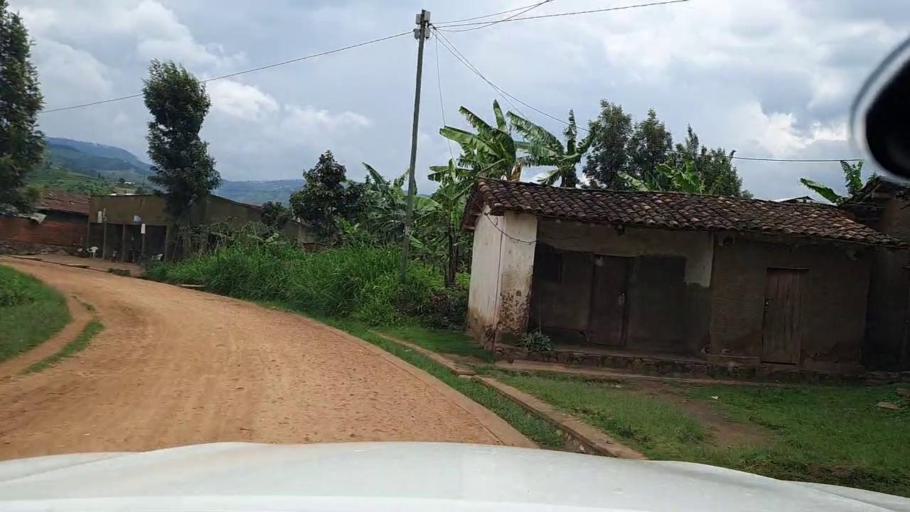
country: RW
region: Western Province
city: Kibuye
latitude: -2.0720
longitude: 29.4286
